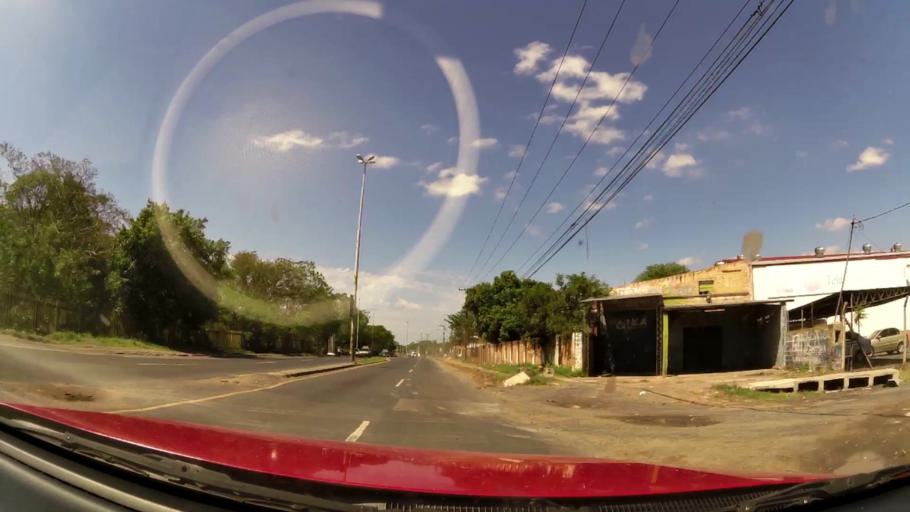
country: PY
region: Asuncion
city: Asuncion
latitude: -25.2547
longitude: -57.5627
